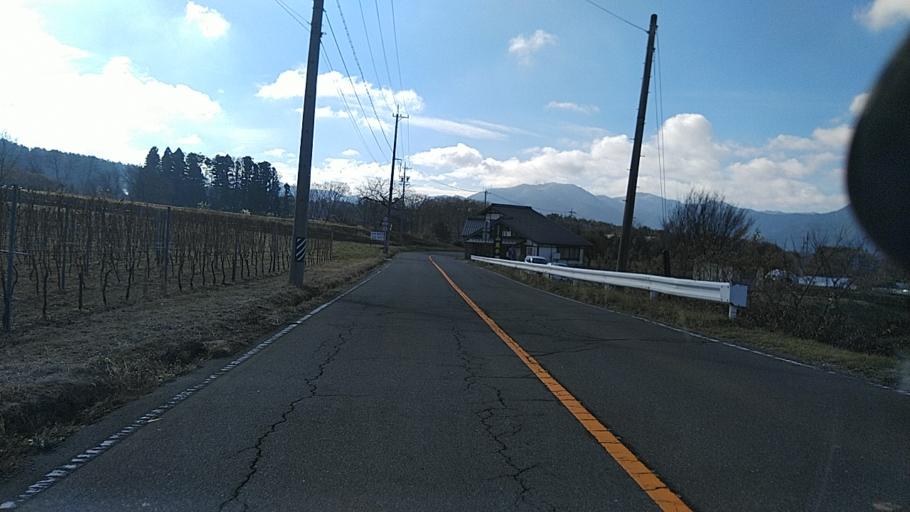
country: JP
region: Nagano
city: Shiojiri
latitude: 36.1285
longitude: 137.9848
